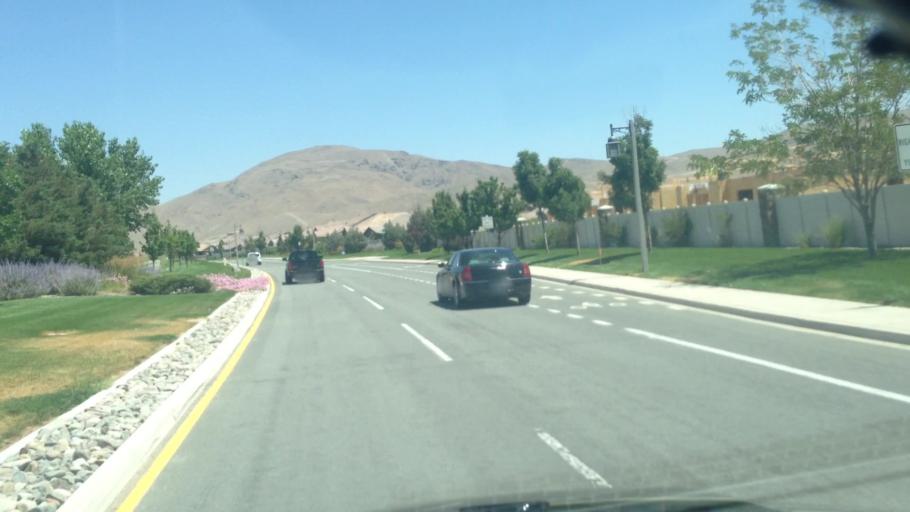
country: US
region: Nevada
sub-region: Washoe County
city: Sparks
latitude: 39.4281
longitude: -119.7305
